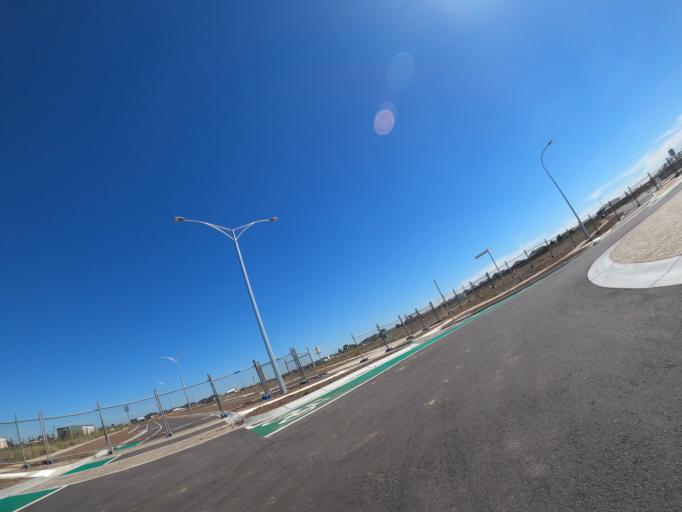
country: AU
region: Victoria
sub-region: Hume
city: Craigieburn
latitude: -37.5318
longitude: 144.9135
